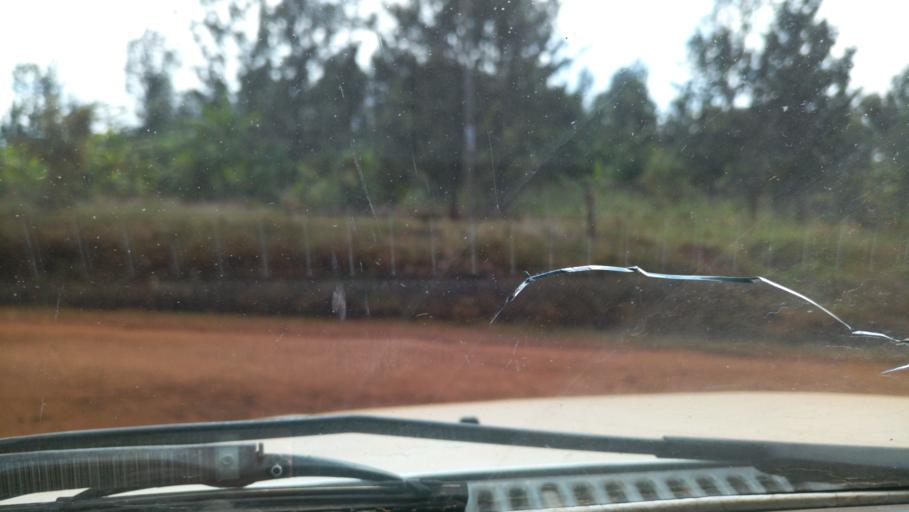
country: KE
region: Murang'a District
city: Maragua
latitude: -0.7653
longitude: 37.1076
